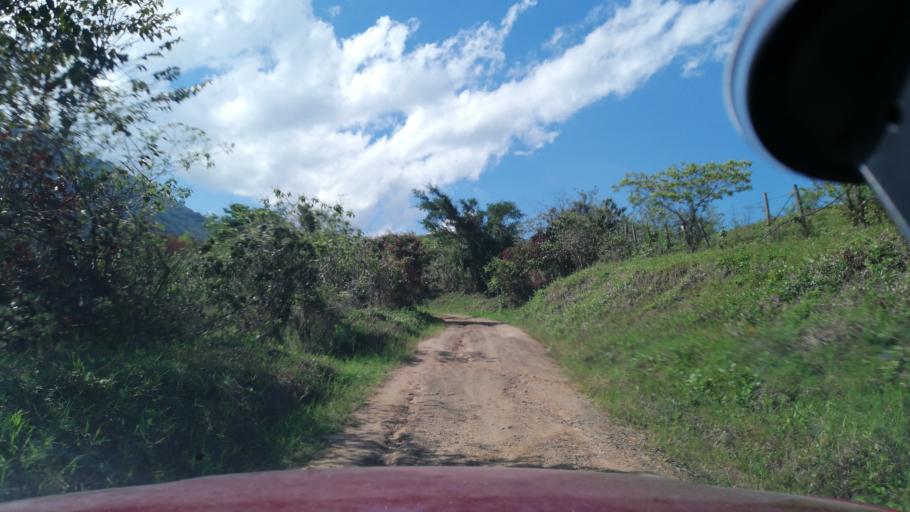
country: CO
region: Cundinamarca
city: Quipile
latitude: 4.7424
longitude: -74.6146
